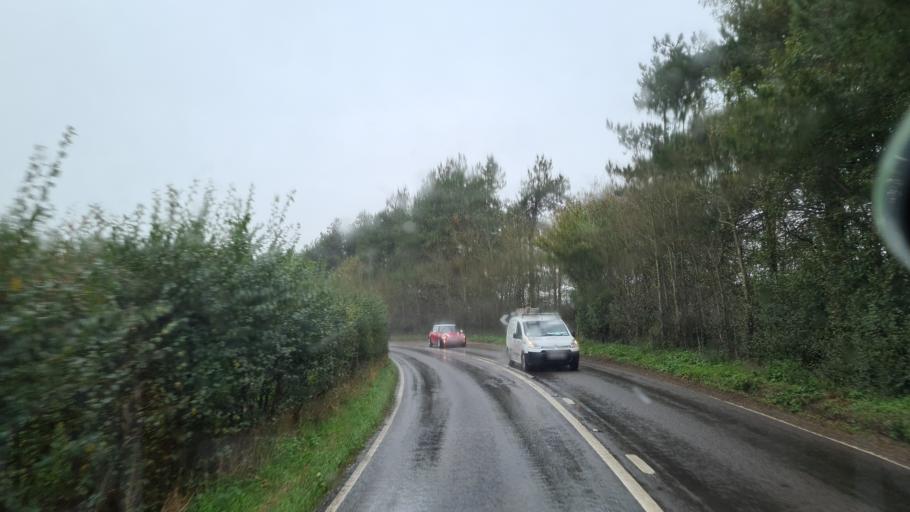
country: GB
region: England
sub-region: West Sussex
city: Washington
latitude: 50.9096
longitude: -0.3909
